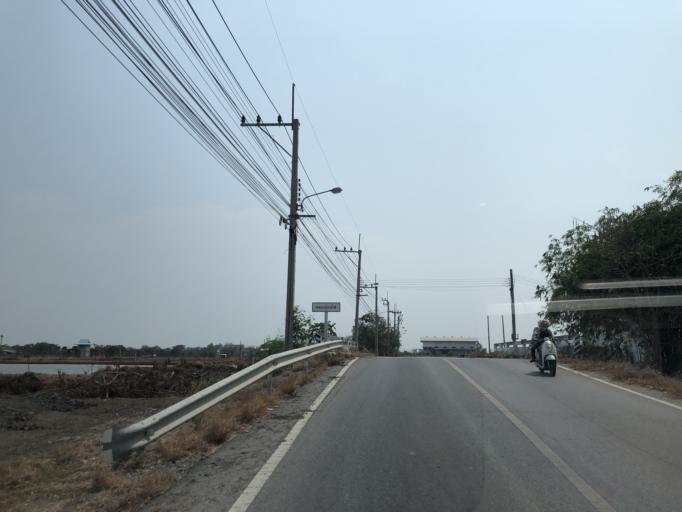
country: TH
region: Samut Prakan
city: Bang Bo
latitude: 13.5397
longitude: 100.8728
